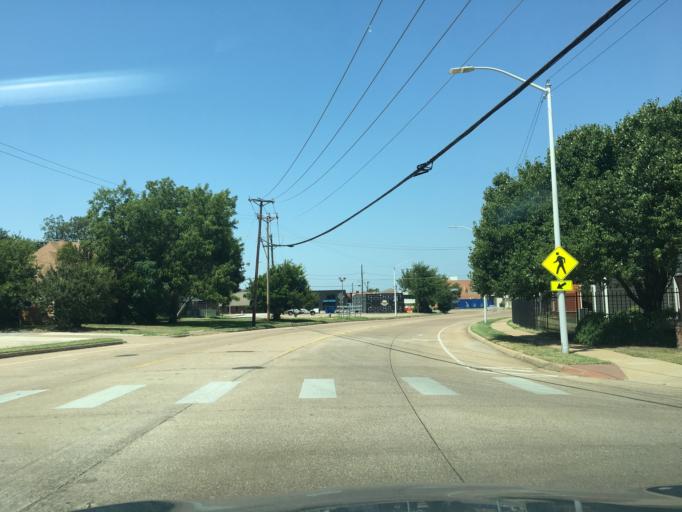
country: US
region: Texas
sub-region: Tarrant County
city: Fort Worth
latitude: 32.7380
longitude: -97.3281
